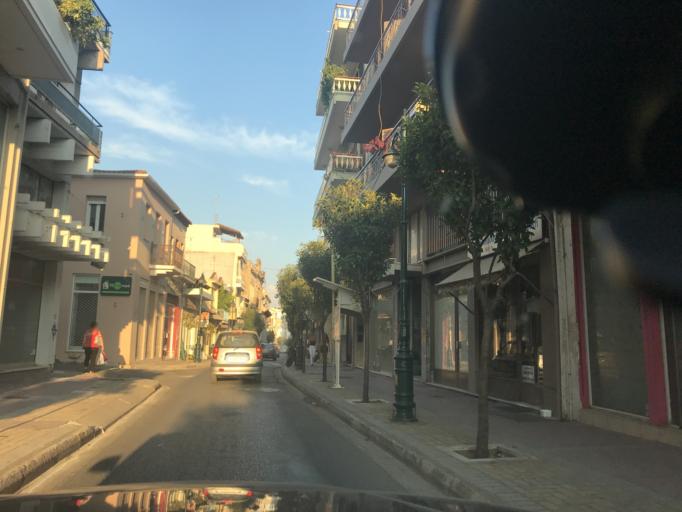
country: GR
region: West Greece
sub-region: Nomos Ileias
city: Pyrgos
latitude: 37.6713
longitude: 21.4426
